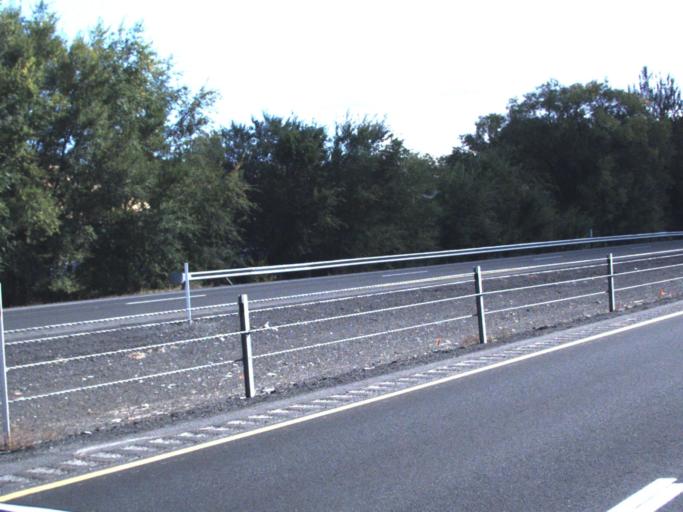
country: US
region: Washington
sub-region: Yakima County
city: Gleed
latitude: 46.6334
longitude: -120.5883
